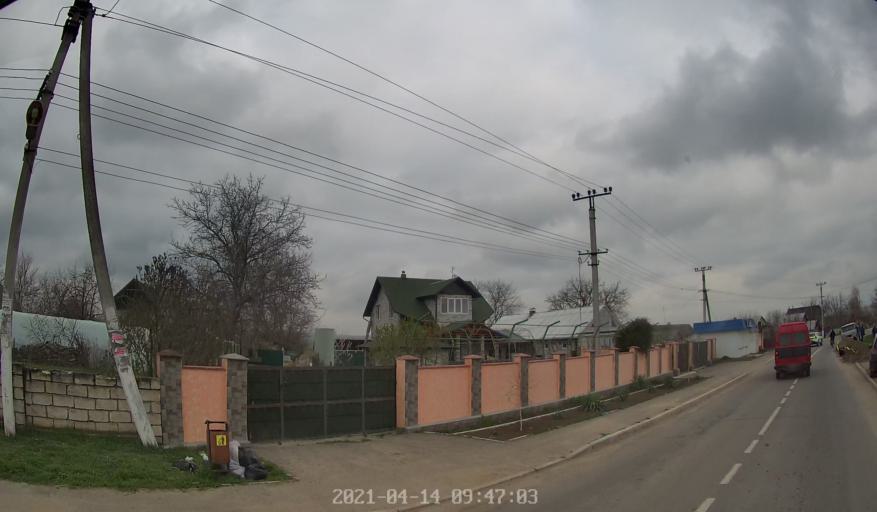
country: MD
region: Chisinau
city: Vadul lui Voda
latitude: 47.1362
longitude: 29.1193
